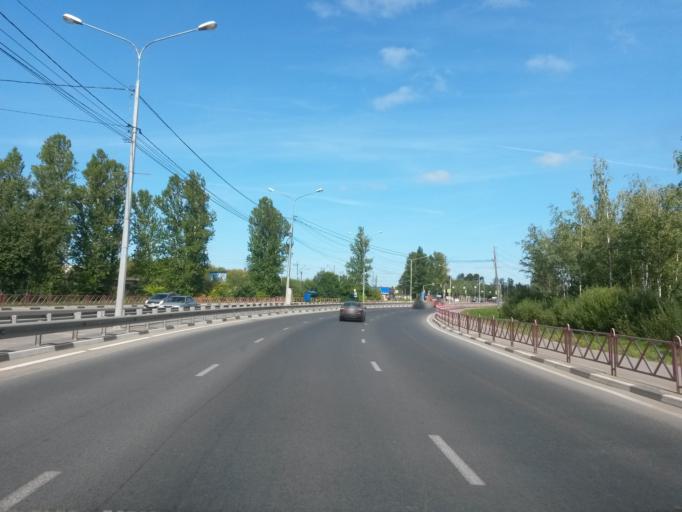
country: RU
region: Jaroslavl
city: Yaroslavl
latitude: 57.5935
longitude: 39.8940
